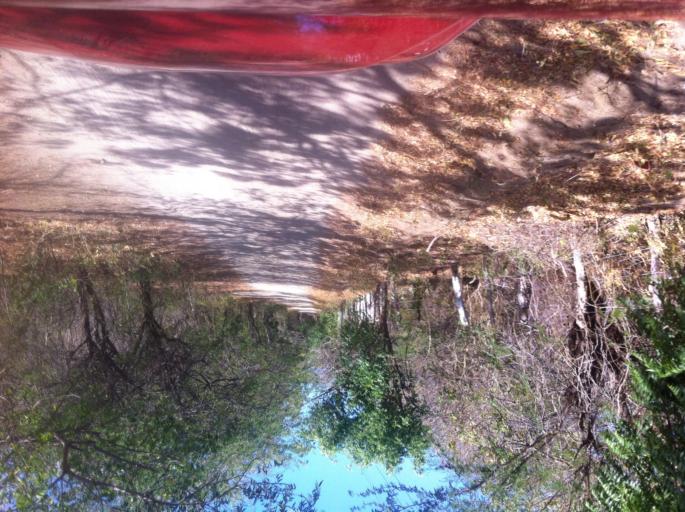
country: NI
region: Carazo
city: Santa Teresa
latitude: 11.6075
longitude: -86.3050
